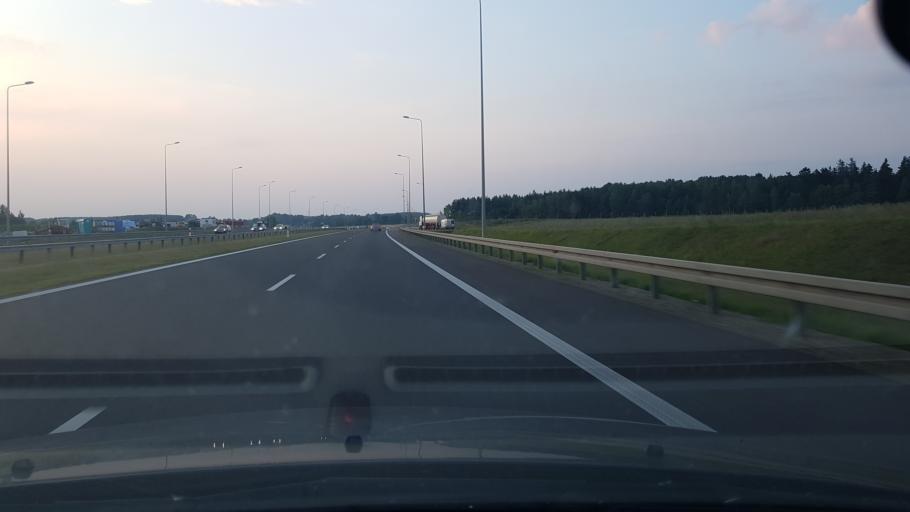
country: PL
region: Warmian-Masurian Voivodeship
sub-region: Powiat nidzicki
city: Nidzica
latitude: 53.2994
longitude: 20.4366
